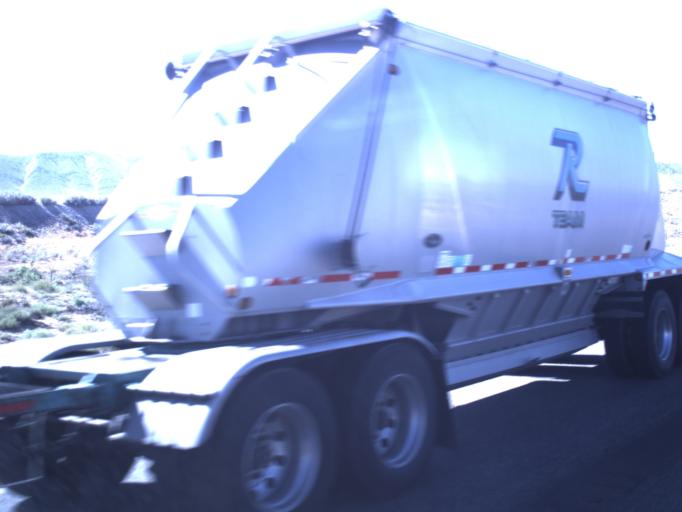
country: US
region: Utah
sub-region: Sevier County
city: Salina
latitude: 39.0141
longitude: -111.8353
